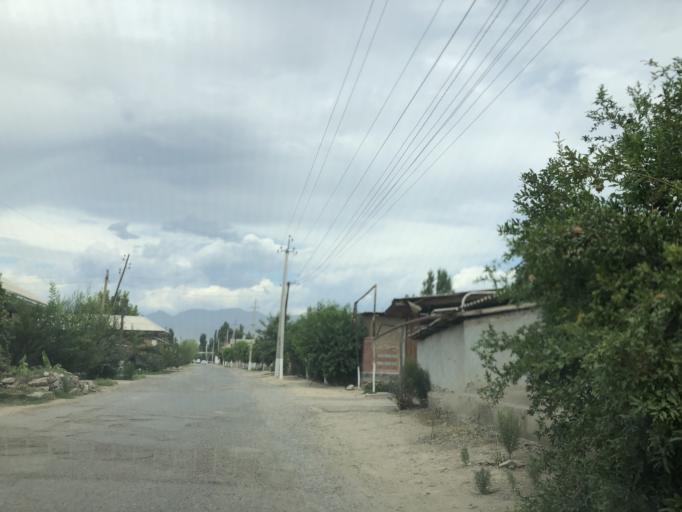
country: UZ
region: Namangan
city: Pop Shahri
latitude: 41.0091
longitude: 71.0895
